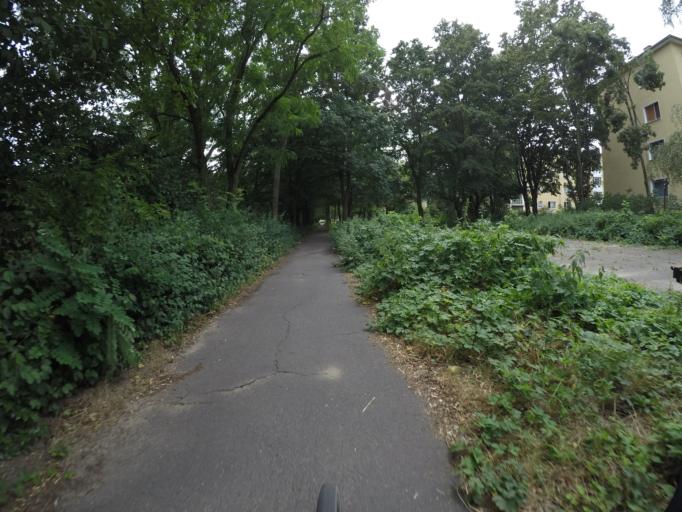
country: DE
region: Berlin
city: Reinickendorf
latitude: 52.5649
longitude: 13.3464
